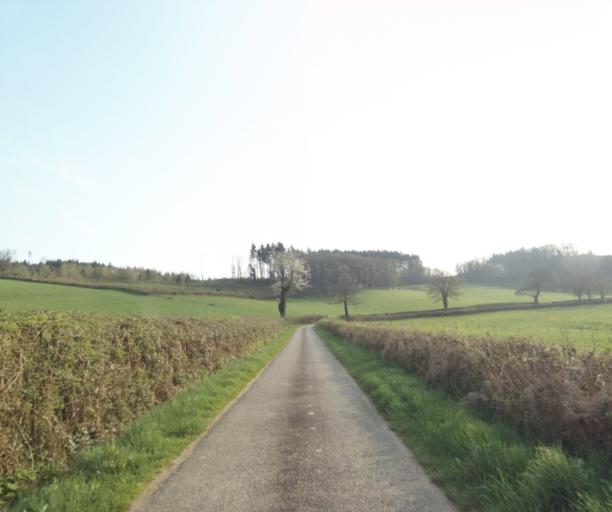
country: FR
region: Bourgogne
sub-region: Departement de Saone-et-Loire
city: Matour
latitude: 46.4203
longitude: 4.4800
